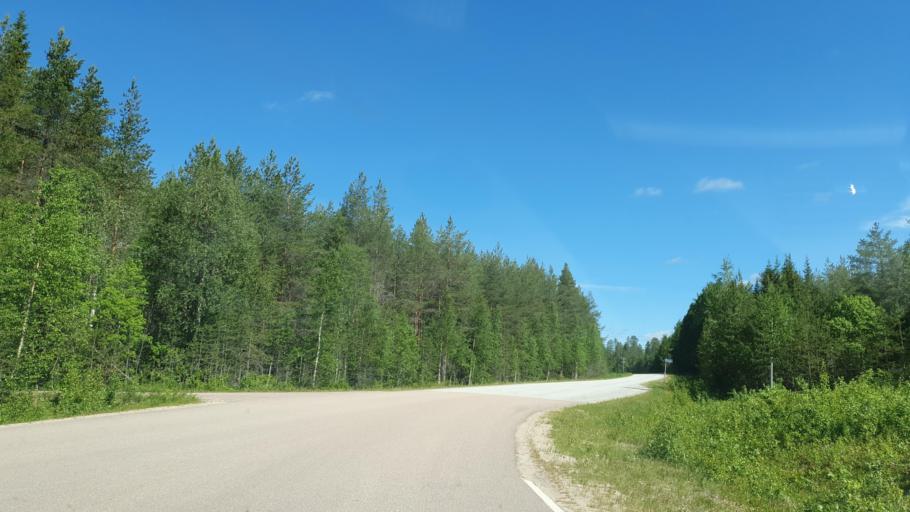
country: FI
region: Kainuu
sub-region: Kehys-Kainuu
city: Kuhmo
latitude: 64.4591
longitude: 29.5321
